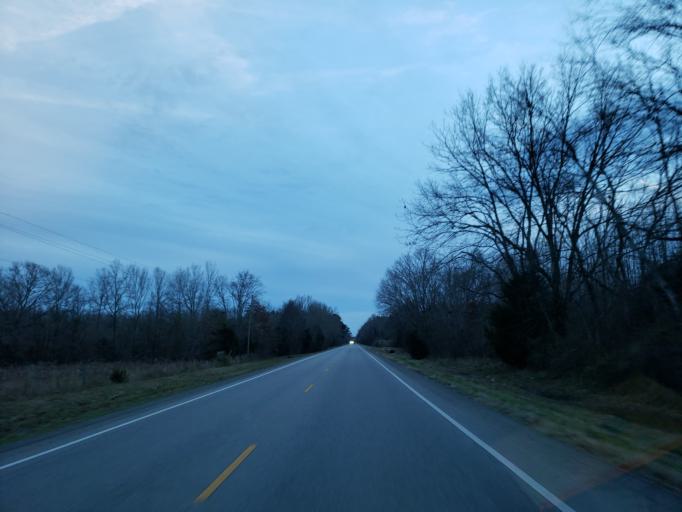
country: US
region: Alabama
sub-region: Sumter County
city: Livingston
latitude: 32.8255
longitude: -88.3099
